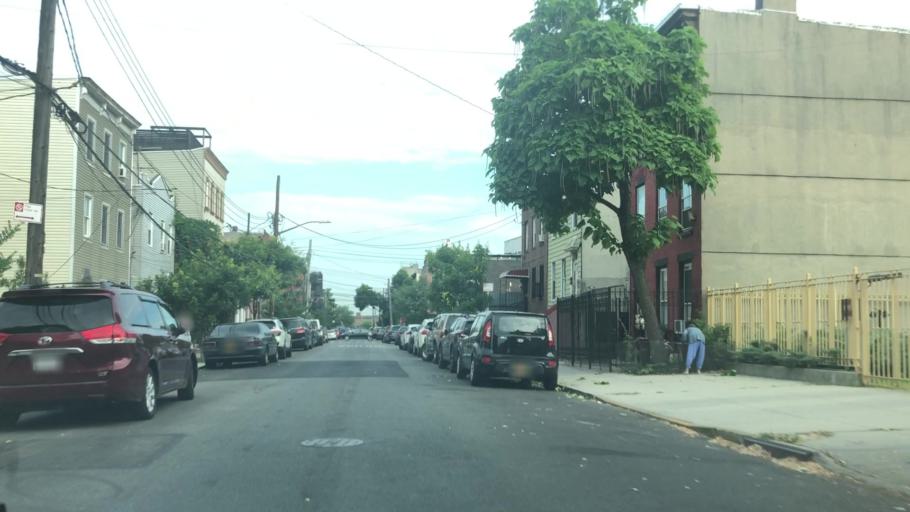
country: US
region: New York
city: New York City
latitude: 40.6763
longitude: -74.0128
